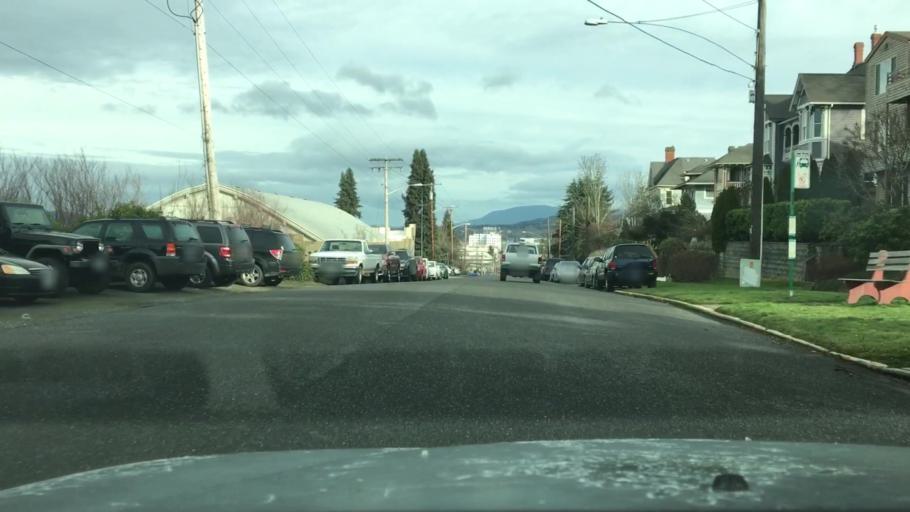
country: US
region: Washington
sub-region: Whatcom County
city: Bellingham
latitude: 48.7403
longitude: -122.4891
